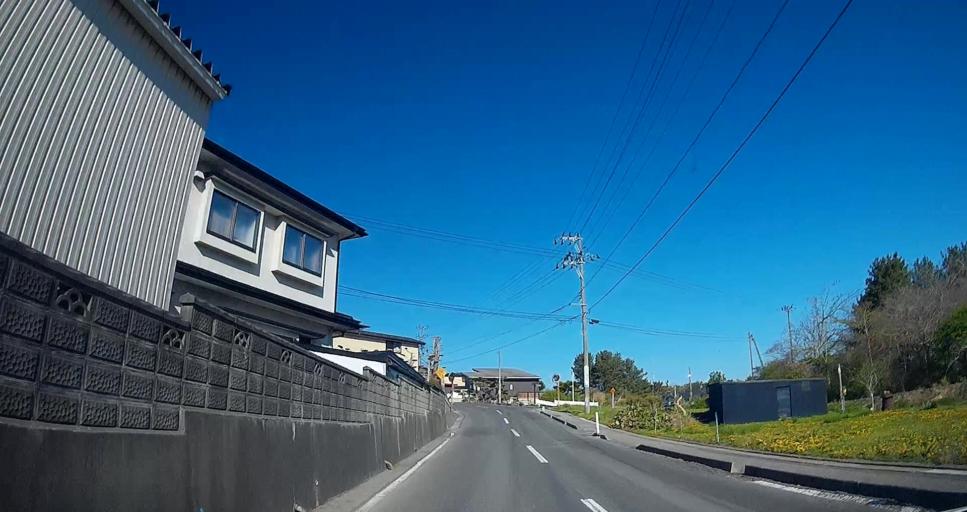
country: JP
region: Aomori
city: Hachinohe
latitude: 40.5150
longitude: 141.5996
